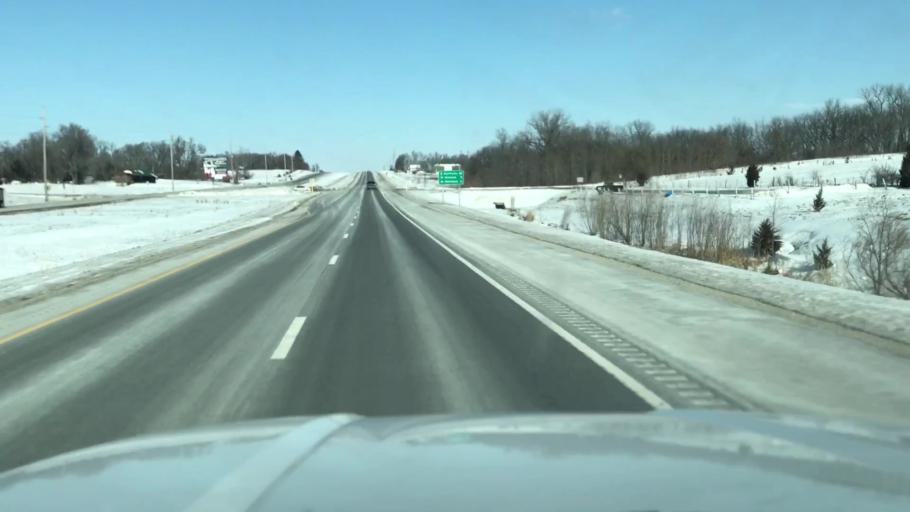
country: US
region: Missouri
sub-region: Nodaway County
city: Maryville
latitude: 40.1985
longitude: -94.8676
